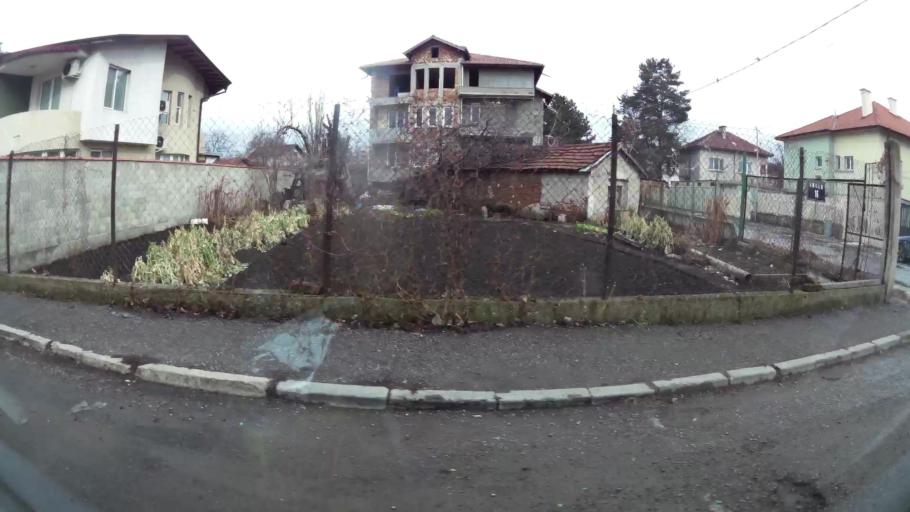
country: BG
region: Sofiya
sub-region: Obshtina Bozhurishte
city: Bozhurishte
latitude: 42.7447
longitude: 23.2649
